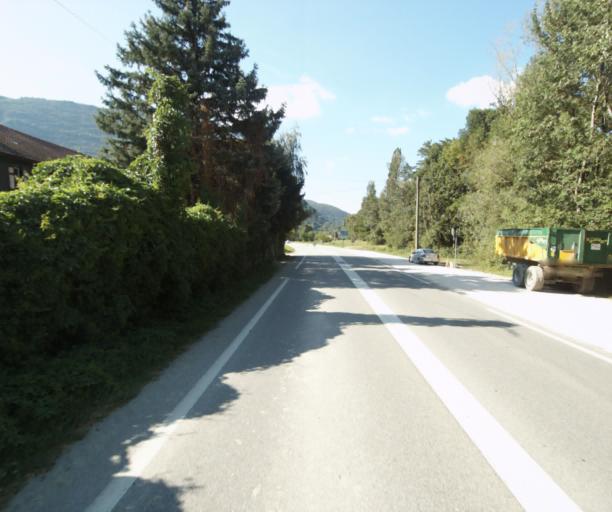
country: FR
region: Rhone-Alpes
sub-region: Departement de l'Isere
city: Veurey-Voroize
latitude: 45.2664
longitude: 5.6222
